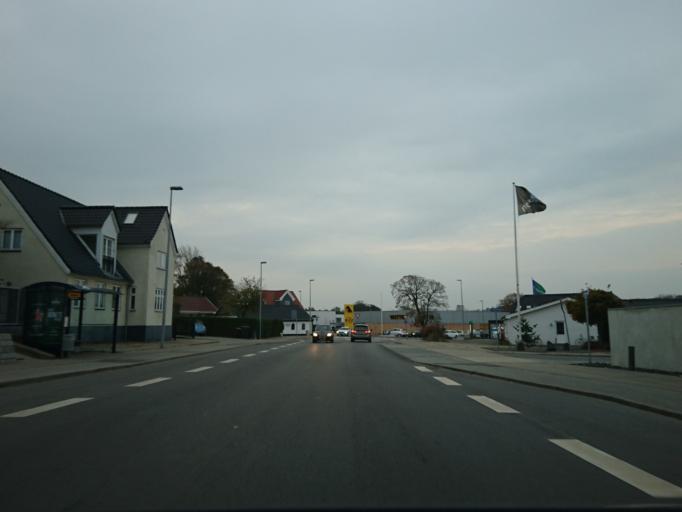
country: DK
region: North Denmark
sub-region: Alborg Kommune
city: Aalborg
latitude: 57.0079
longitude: 9.9266
